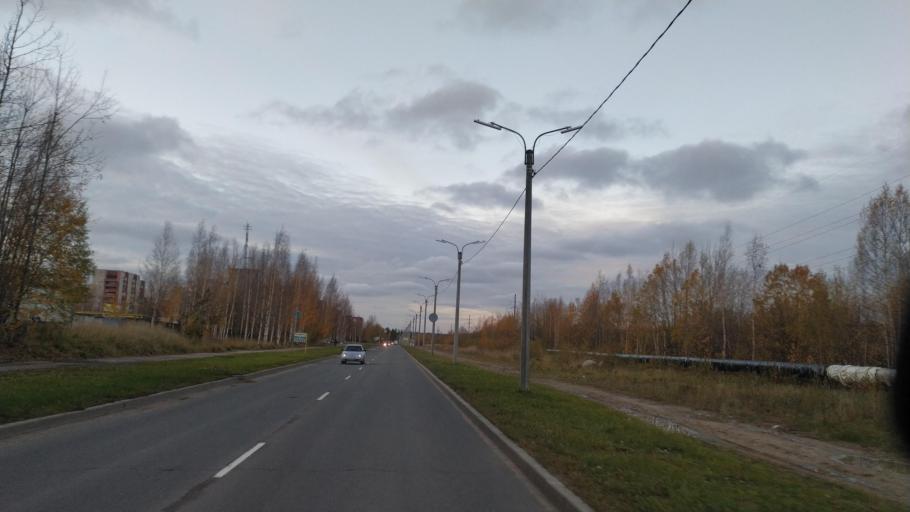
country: RU
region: Leningrad
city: Sosnovyy Bor
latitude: 59.9097
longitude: 29.1004
